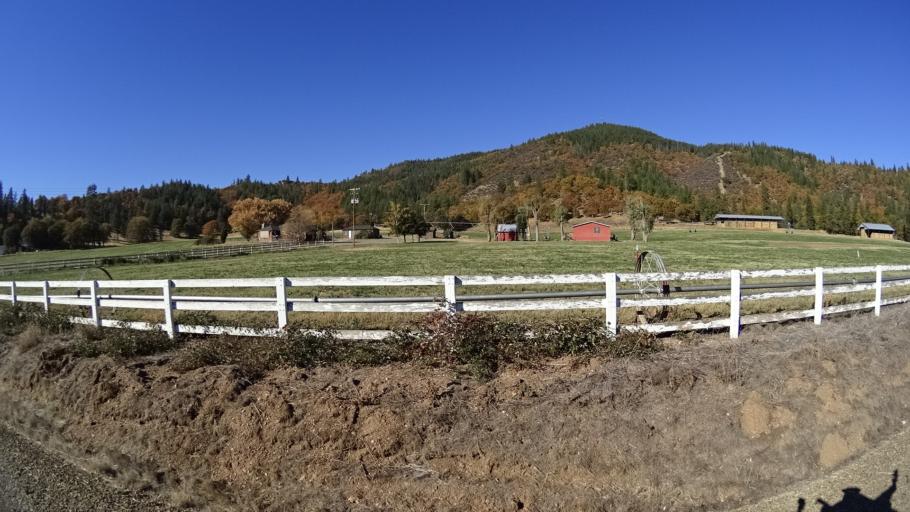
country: US
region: California
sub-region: Siskiyou County
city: Yreka
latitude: 41.5918
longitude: -122.8584
